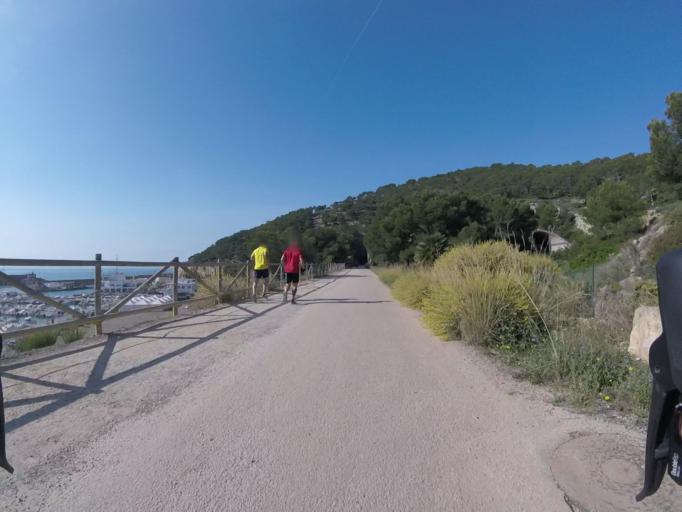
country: ES
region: Valencia
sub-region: Provincia de Castello
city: Orpesa/Oropesa del Mar
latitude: 40.0767
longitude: 0.1324
